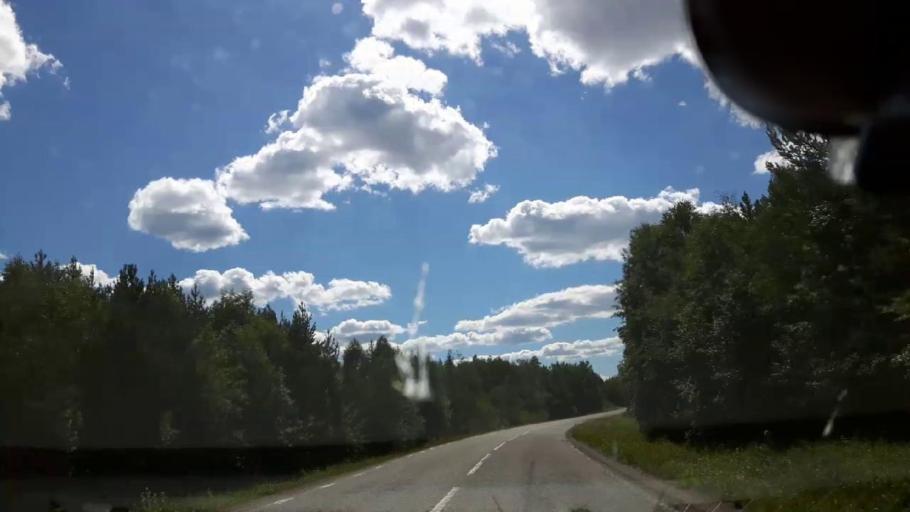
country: SE
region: Jaemtland
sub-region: Ragunda Kommun
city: Hammarstrand
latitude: 63.0387
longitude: 16.3911
